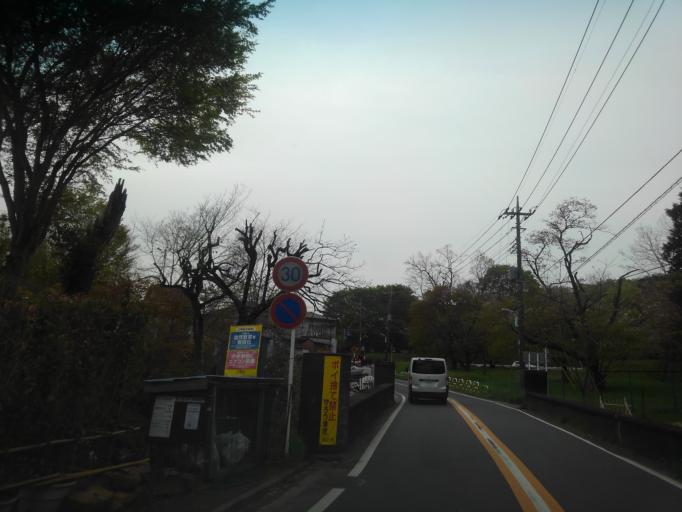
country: JP
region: Tokyo
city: Higashimurayama-shi
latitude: 35.7762
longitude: 139.4179
